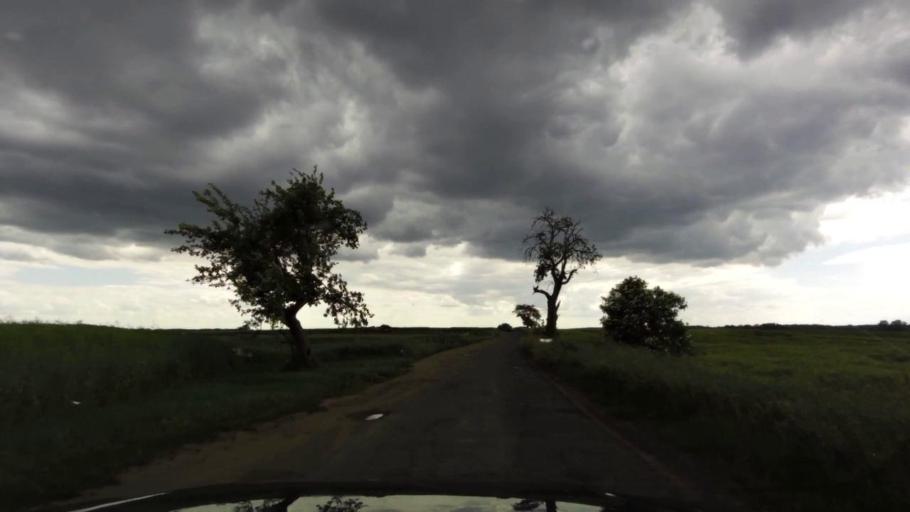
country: PL
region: West Pomeranian Voivodeship
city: Trzcinsko Zdroj
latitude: 52.9537
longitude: 14.6076
